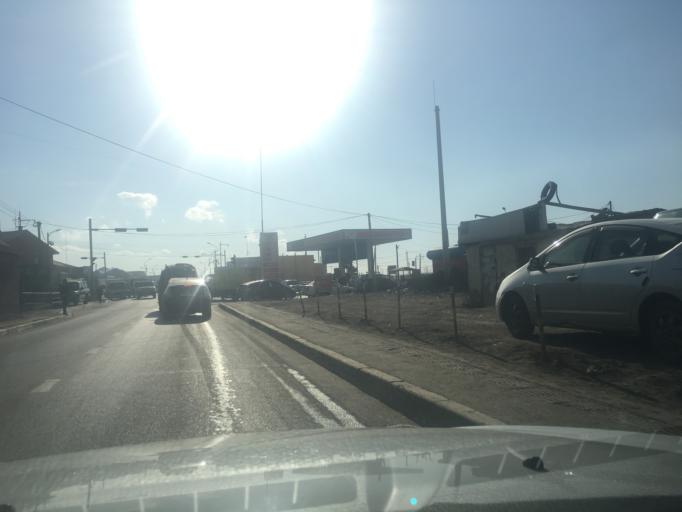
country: MN
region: Ulaanbaatar
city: Ulaanbaatar
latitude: 47.9573
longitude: 106.8264
